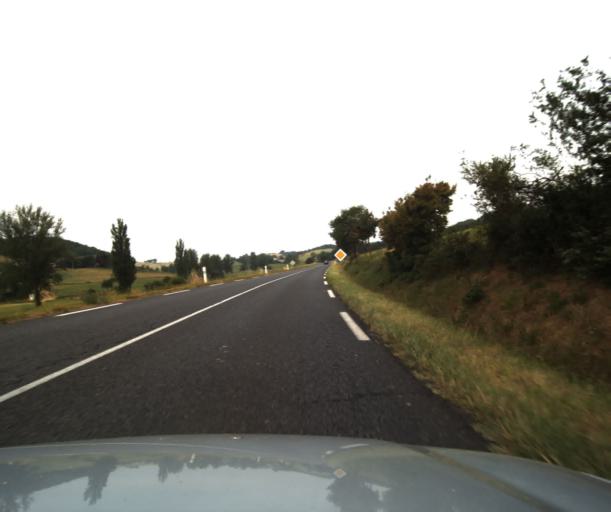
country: FR
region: Midi-Pyrenees
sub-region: Departement du Gers
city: Pavie
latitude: 43.5625
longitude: 0.5086
